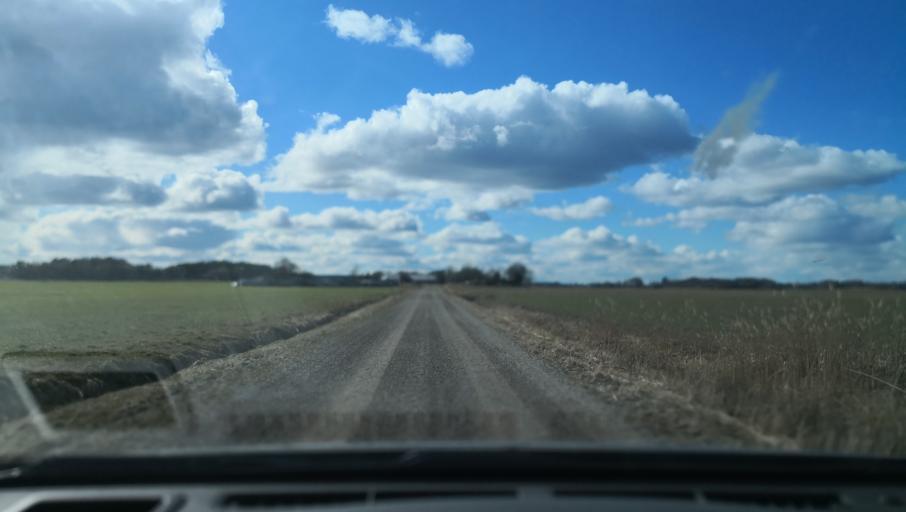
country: SE
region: OErebro
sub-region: Lindesbergs Kommun
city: Fellingsbro
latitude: 59.4125
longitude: 15.6661
